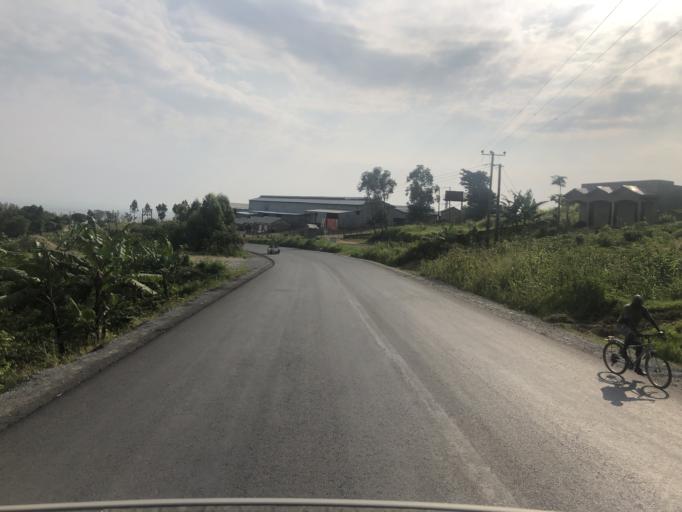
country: UG
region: Western Region
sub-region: Rubirizi District
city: Rubirizi
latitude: -0.2218
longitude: 30.0975
